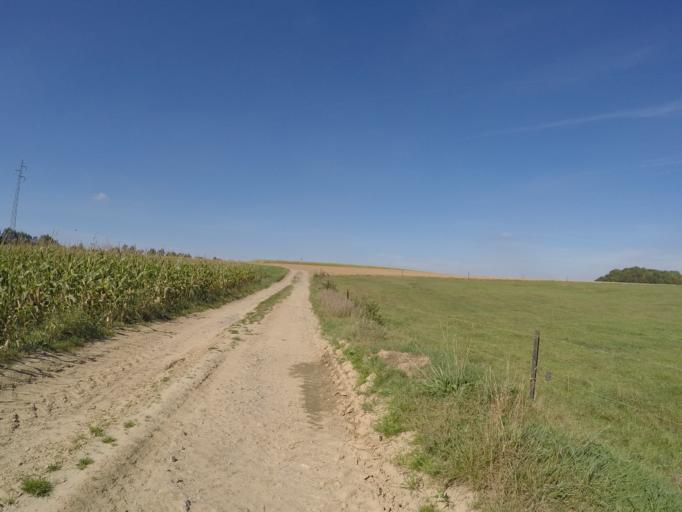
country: BE
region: Wallonia
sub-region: Province de Namur
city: Assesse
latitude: 50.3052
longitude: 5.0235
